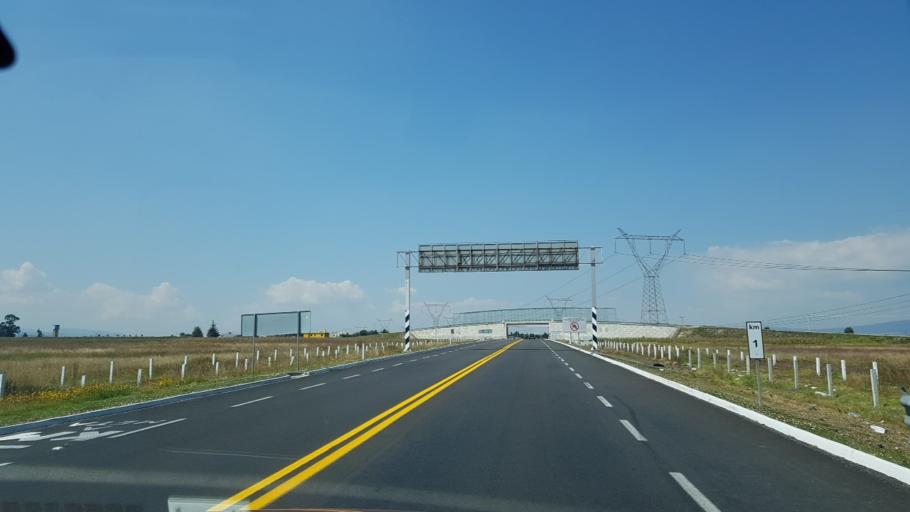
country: MX
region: Mexico
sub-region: Toluca
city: Sebastian Lerdo de Tejada
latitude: 19.3873
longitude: -99.7179
